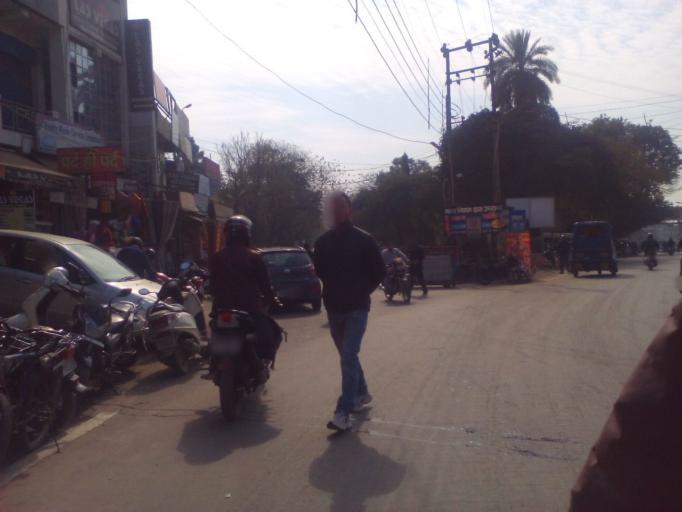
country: IN
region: Uttarakhand
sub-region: Dehradun
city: Dehradun
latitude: 30.3223
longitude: 78.0424
